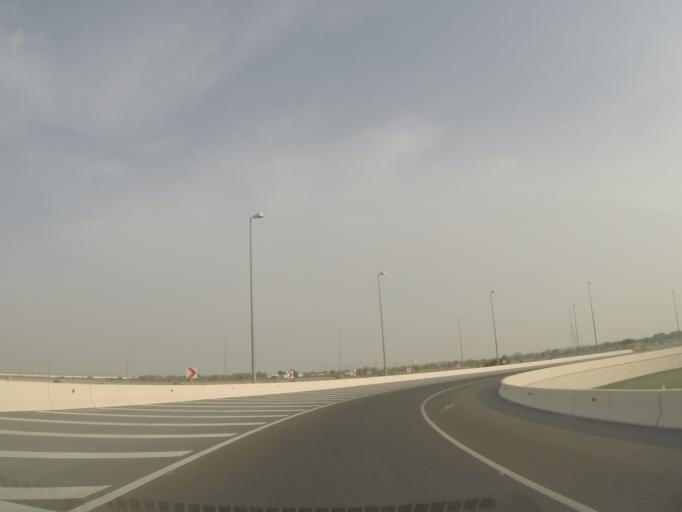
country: AE
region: Abu Dhabi
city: Abu Dhabi
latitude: 24.6929
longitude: 54.7808
